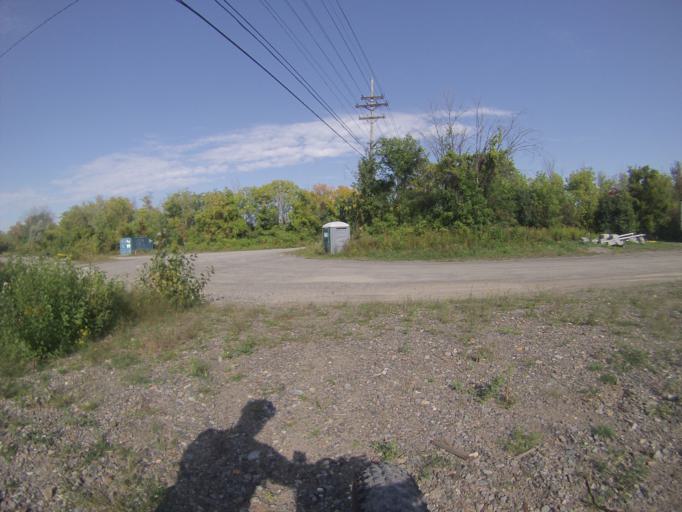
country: CA
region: Ontario
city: Ottawa
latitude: 45.3667
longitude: -75.6500
